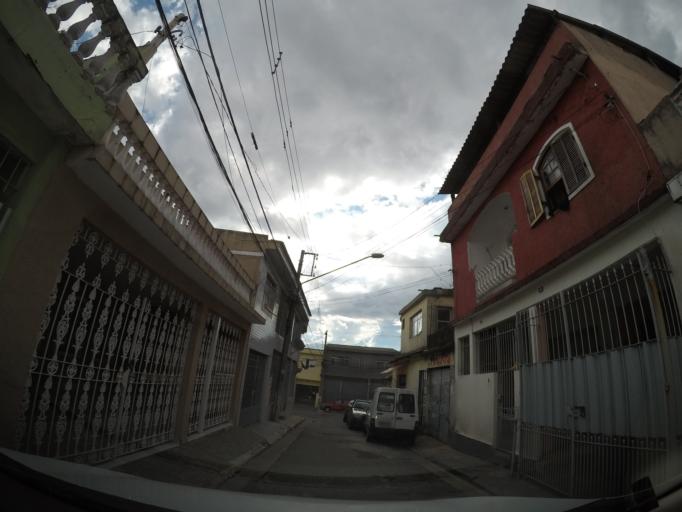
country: BR
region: Sao Paulo
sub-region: Guarulhos
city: Guarulhos
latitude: -23.4787
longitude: -46.5536
